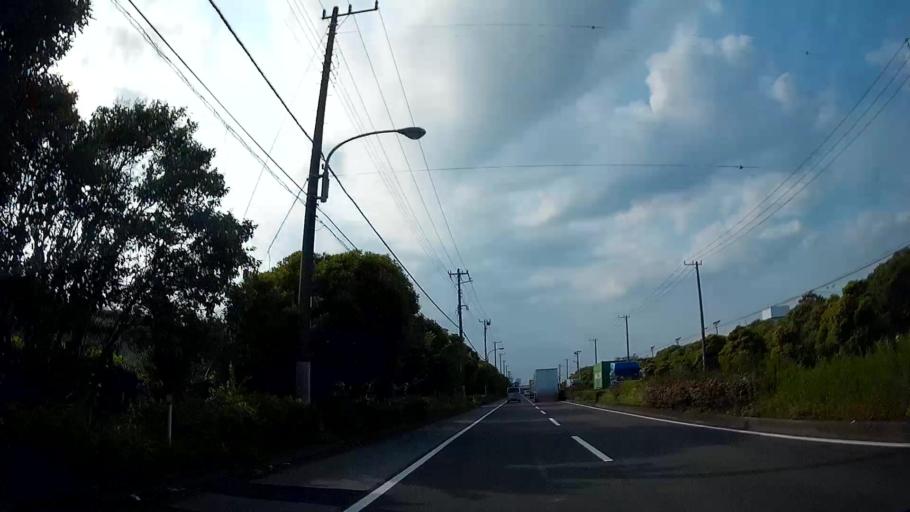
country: JP
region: Chiba
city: Funabashi
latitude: 35.6715
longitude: 140.0018
